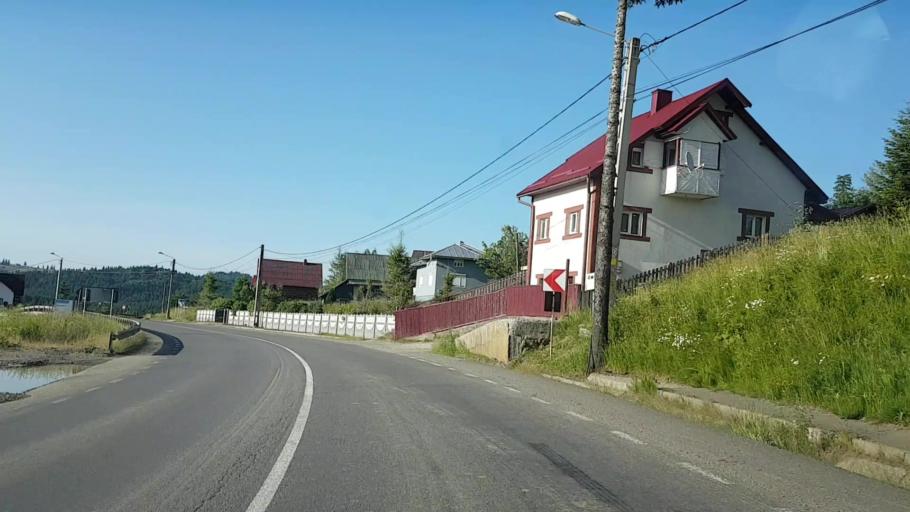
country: RO
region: Bistrita-Nasaud
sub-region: Comuna Lunca Ilvei
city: Lunca Ilvei
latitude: 47.2395
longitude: 25.0081
